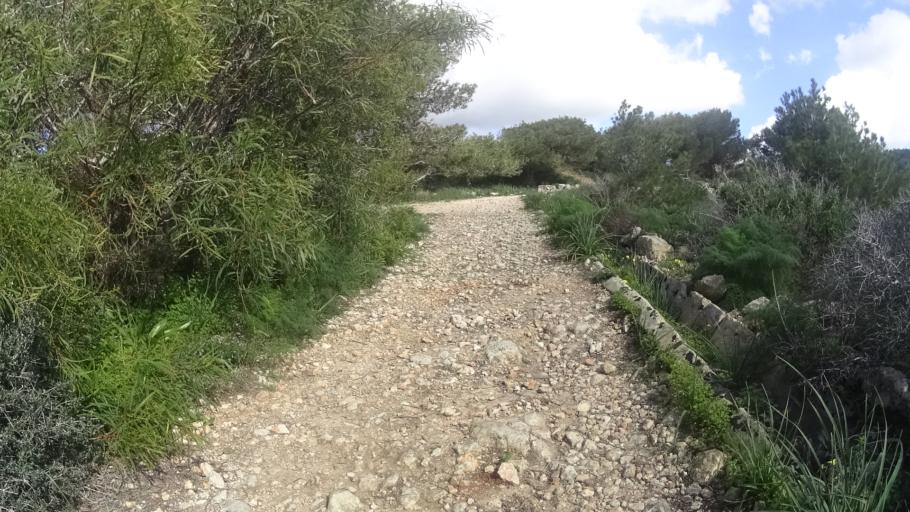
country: MT
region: L-Imgarr
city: Imgarr
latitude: 35.9050
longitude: 14.3796
